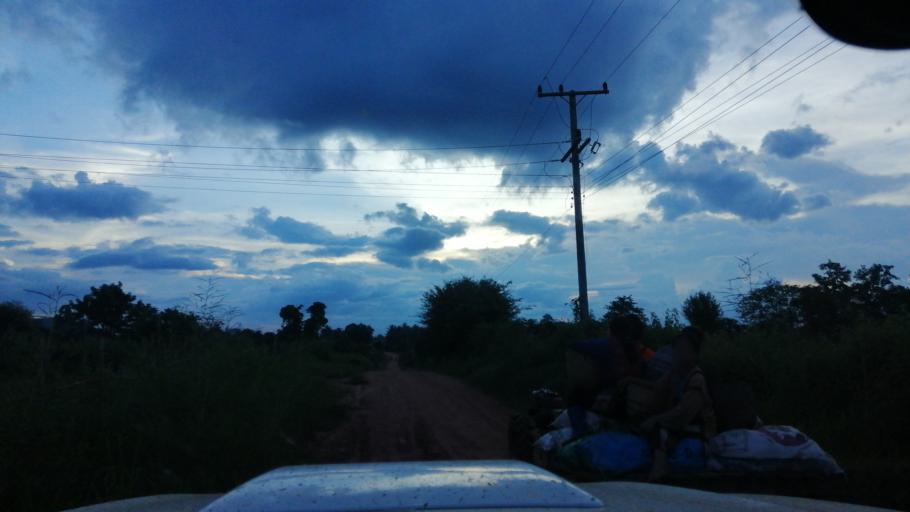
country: TH
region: Uttaradit
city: Ban Khok
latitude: 17.8779
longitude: 101.0529
